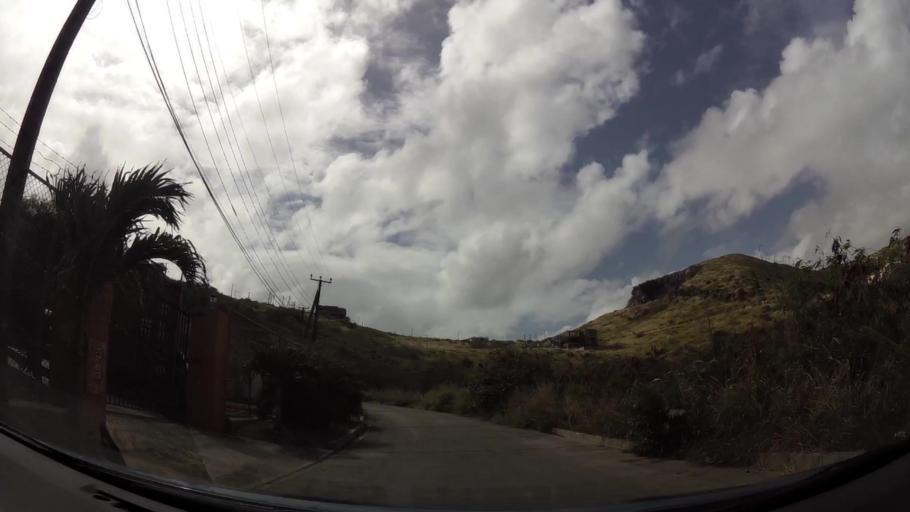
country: KN
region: Saint Peter Basseterre
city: Monkey Hill
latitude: 17.3075
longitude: -62.6949
